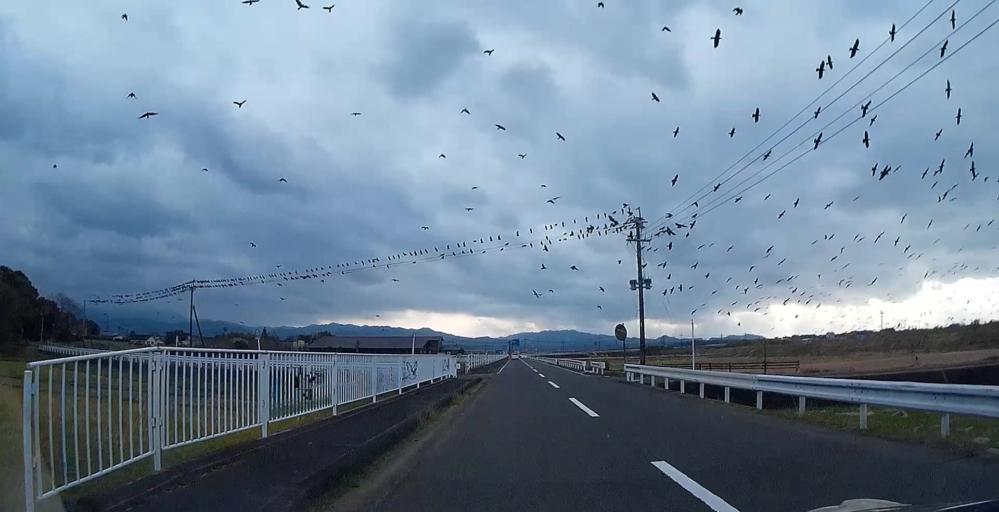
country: JP
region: Kagoshima
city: Izumi
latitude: 32.0865
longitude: 130.2763
